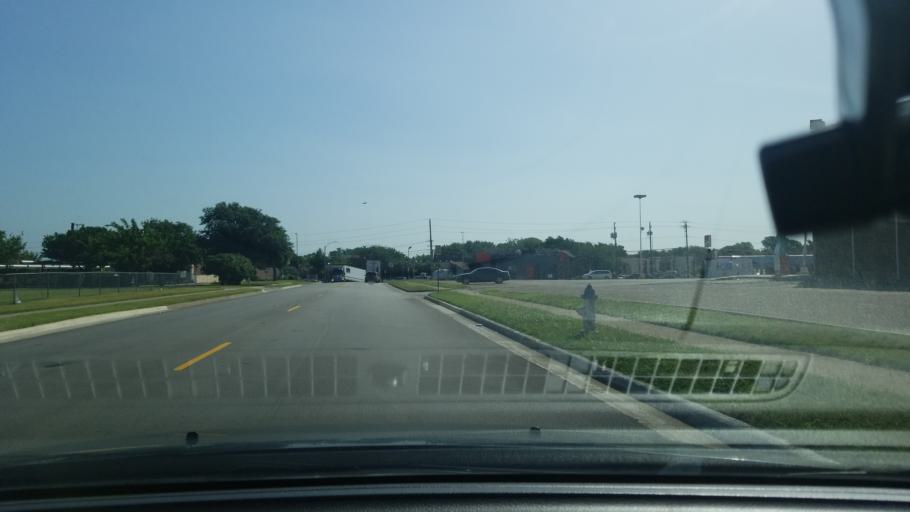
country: US
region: Texas
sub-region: Dallas County
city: Mesquite
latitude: 32.8084
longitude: -96.6848
